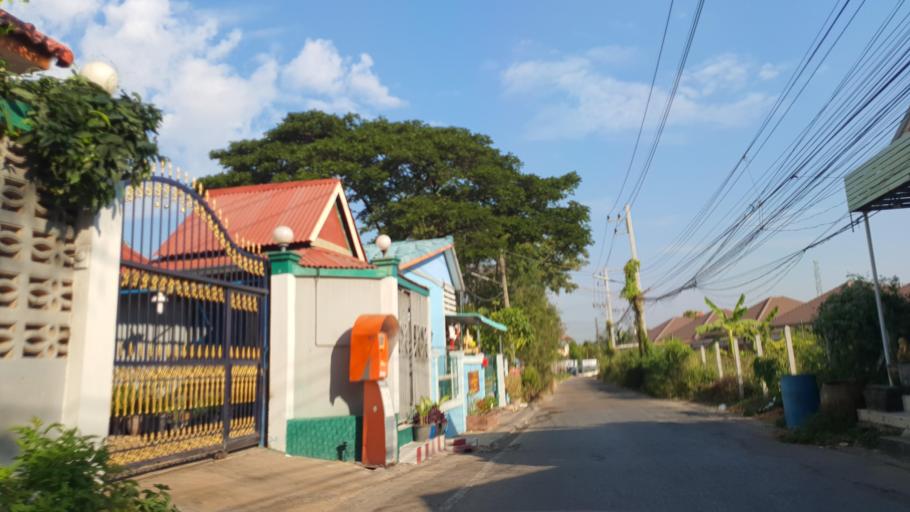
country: TH
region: Khon Kaen
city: Khon Kaen
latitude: 16.4133
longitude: 102.8068
